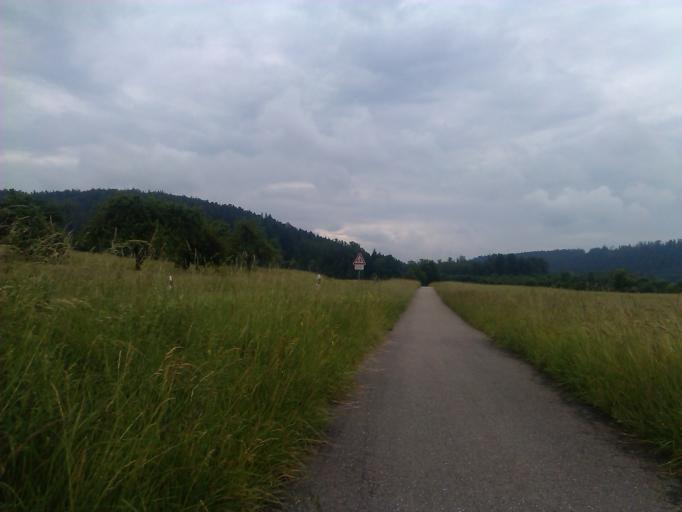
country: DE
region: Baden-Wuerttemberg
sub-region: Regierungsbezirk Stuttgart
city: Oberrot
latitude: 48.9996
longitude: 9.6850
